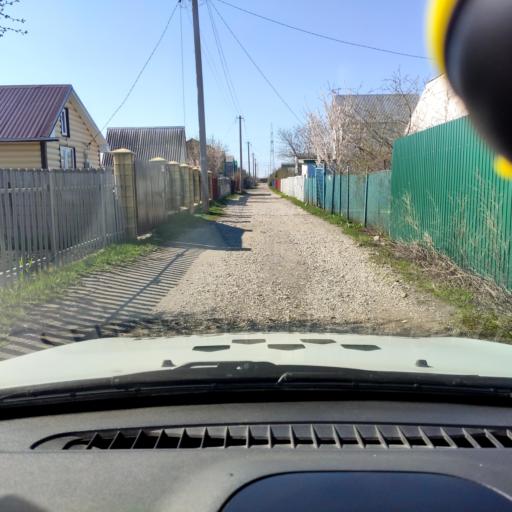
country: RU
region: Samara
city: Tol'yatti
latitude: 53.5937
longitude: 49.2936
